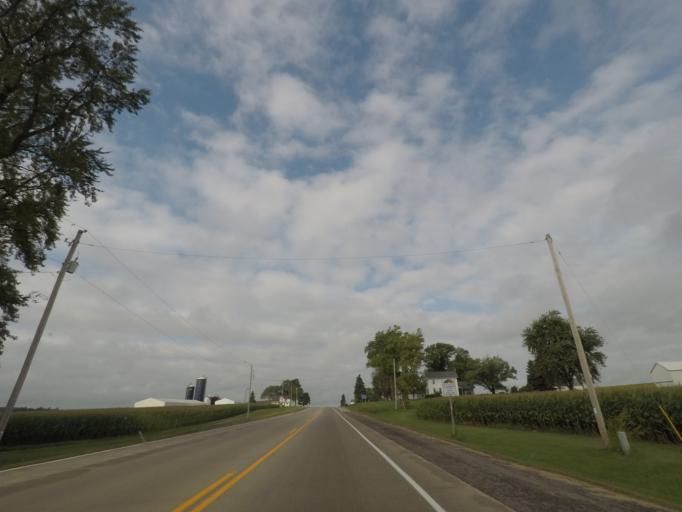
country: US
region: Wisconsin
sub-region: Dane County
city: Cottage Grove
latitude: 43.0308
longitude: -89.1504
